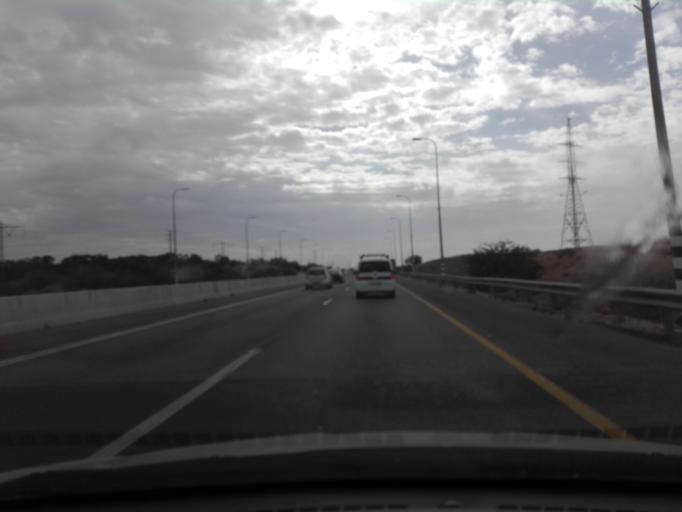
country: IL
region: Southern District
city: Lehavim
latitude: 31.3200
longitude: 34.7870
